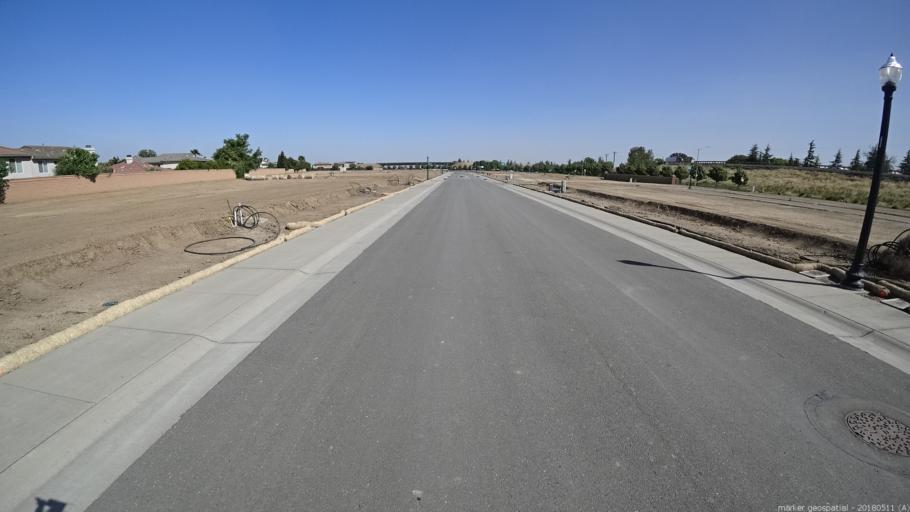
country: US
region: California
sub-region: Yolo County
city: West Sacramento
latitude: 38.6651
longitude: -121.5409
